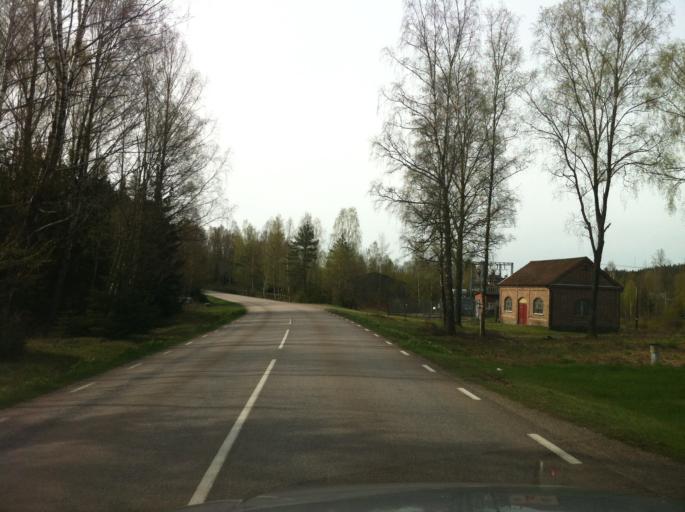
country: SE
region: Vaestra Goetaland
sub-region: Bollebygds Kommun
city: Bollebygd
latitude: 57.7226
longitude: 12.5852
